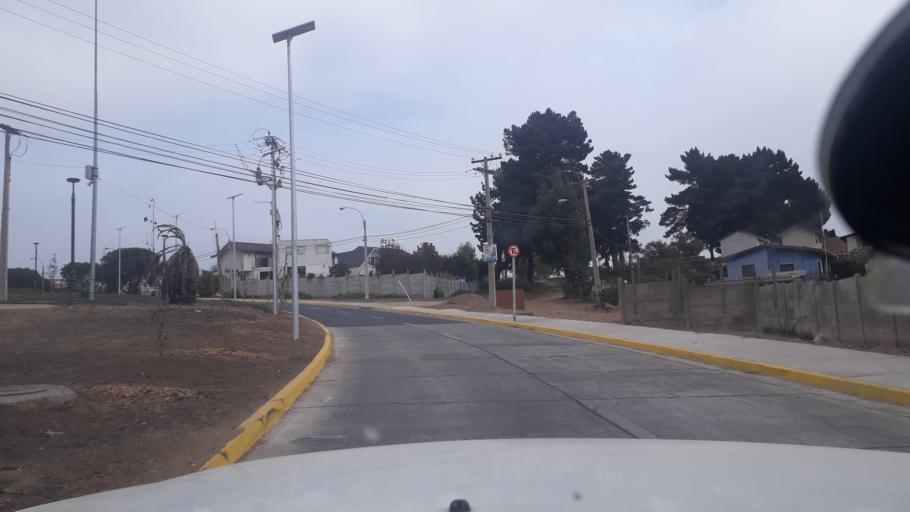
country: CL
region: Valparaiso
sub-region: Provincia de Valparaiso
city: Vina del Mar
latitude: -32.9383
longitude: -71.5367
